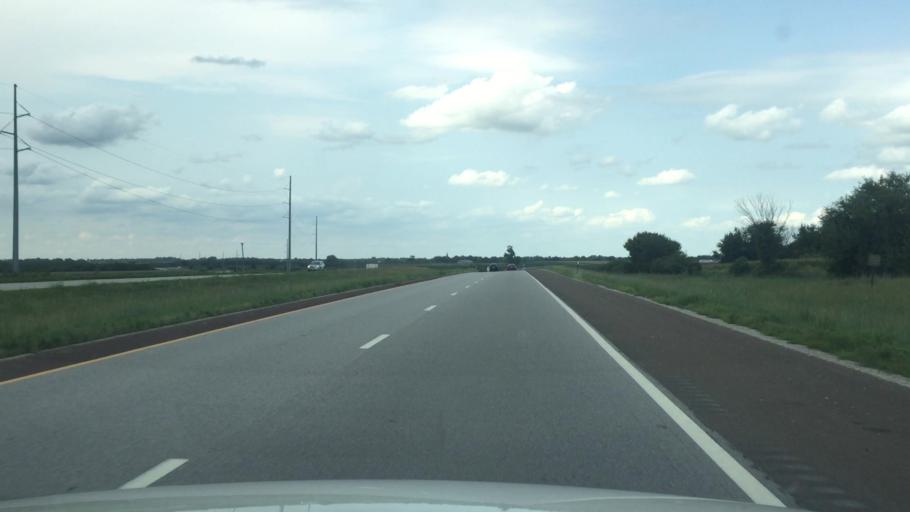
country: US
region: Kansas
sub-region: Miami County
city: Louisburg
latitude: 38.6924
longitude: -94.6786
